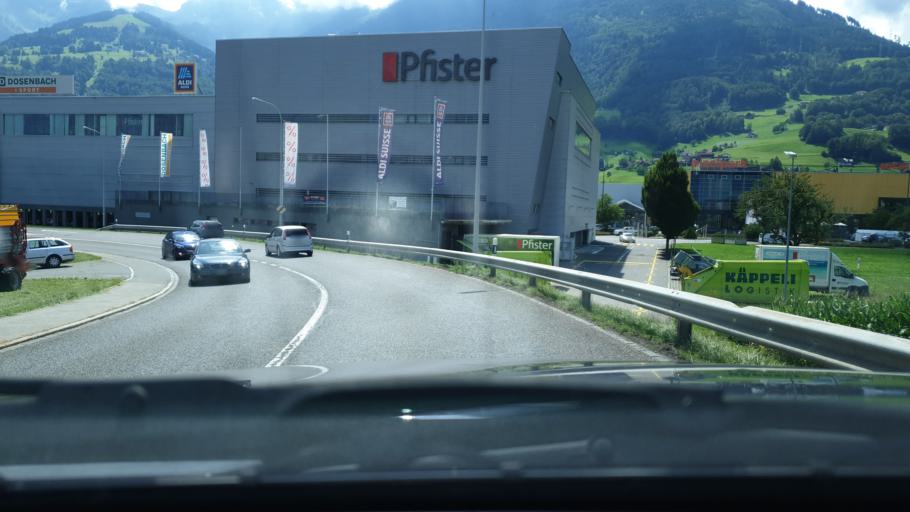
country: CH
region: Saint Gallen
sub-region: Wahlkreis Sarganserland
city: Sargans
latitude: 47.0429
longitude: 9.4341
